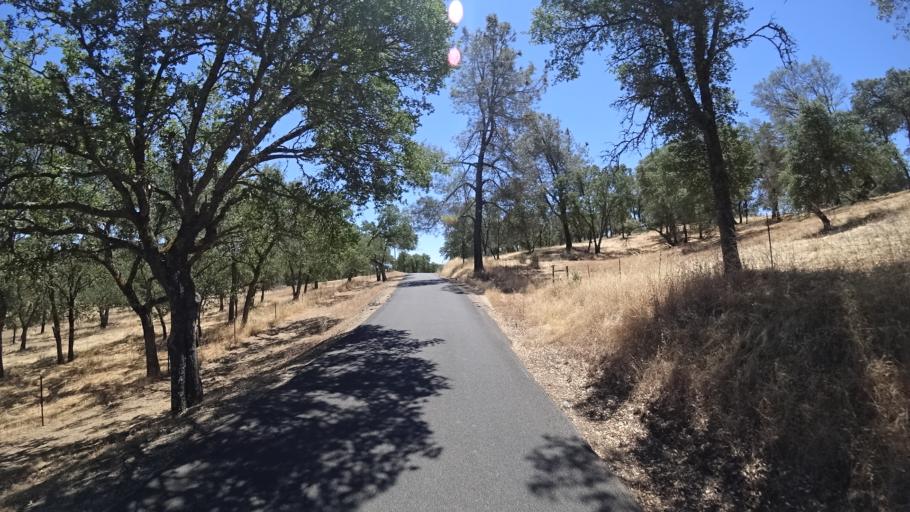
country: US
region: California
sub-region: Calaveras County
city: Copperopolis
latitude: 37.9801
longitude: -120.6791
